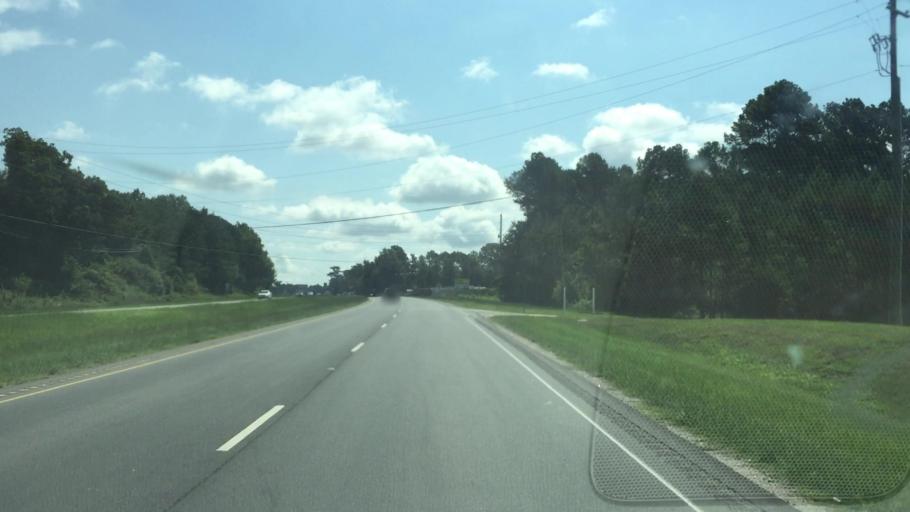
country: US
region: North Carolina
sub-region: Anson County
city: Wadesboro
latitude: 34.9785
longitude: -80.1097
